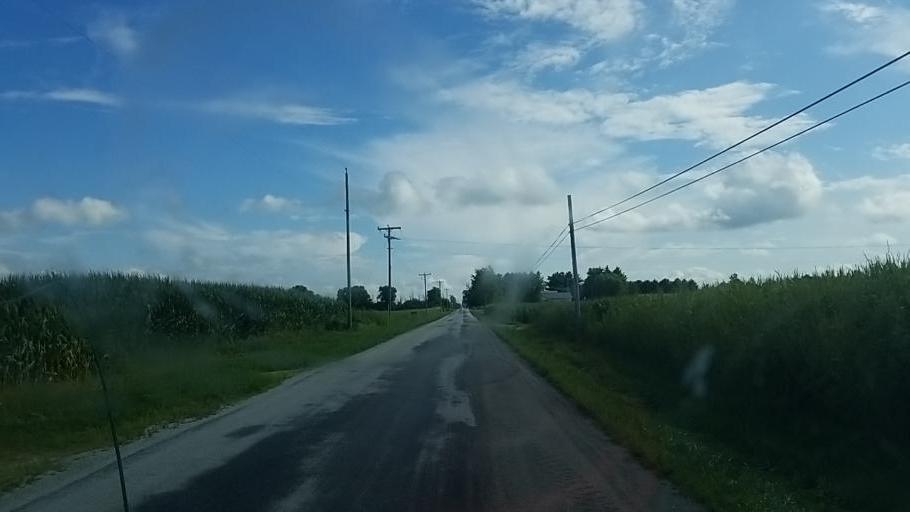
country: US
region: Ohio
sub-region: Hardin County
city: Kenton
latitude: 40.6787
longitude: -83.5380
